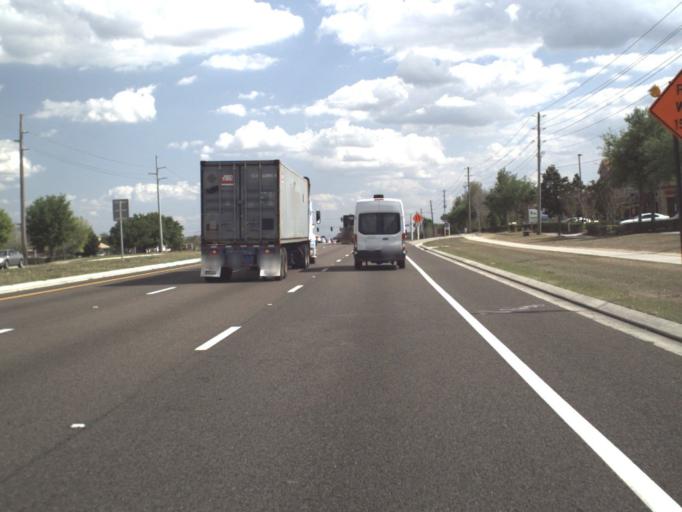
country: US
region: Florida
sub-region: Lake County
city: Clermont
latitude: 28.5026
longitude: -81.7200
